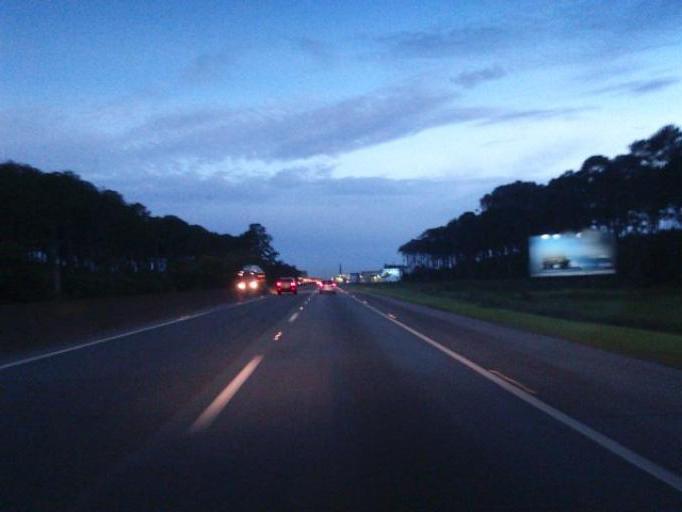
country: BR
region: Santa Catarina
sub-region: Barra Velha
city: Barra Velha
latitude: -26.5080
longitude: -48.7251
